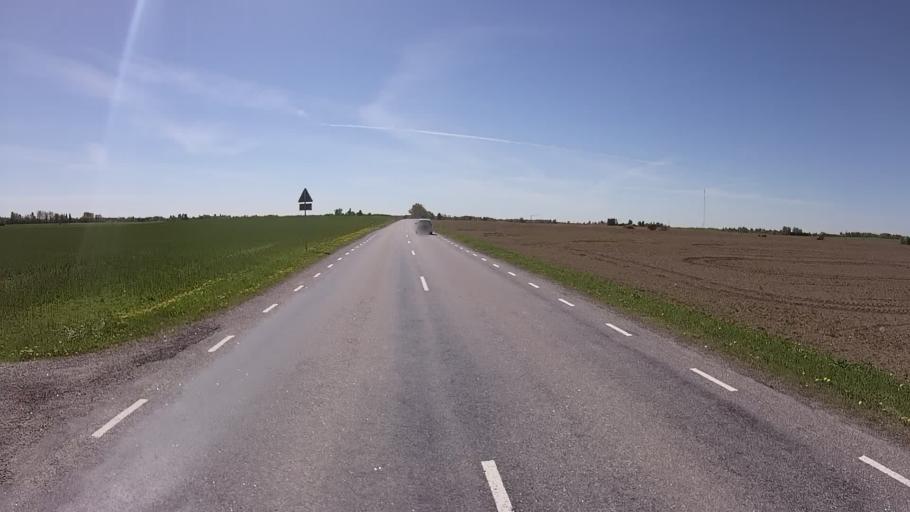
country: EE
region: Raplamaa
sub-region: Kehtna vald
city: Kehtna
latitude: 59.0546
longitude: 25.1344
